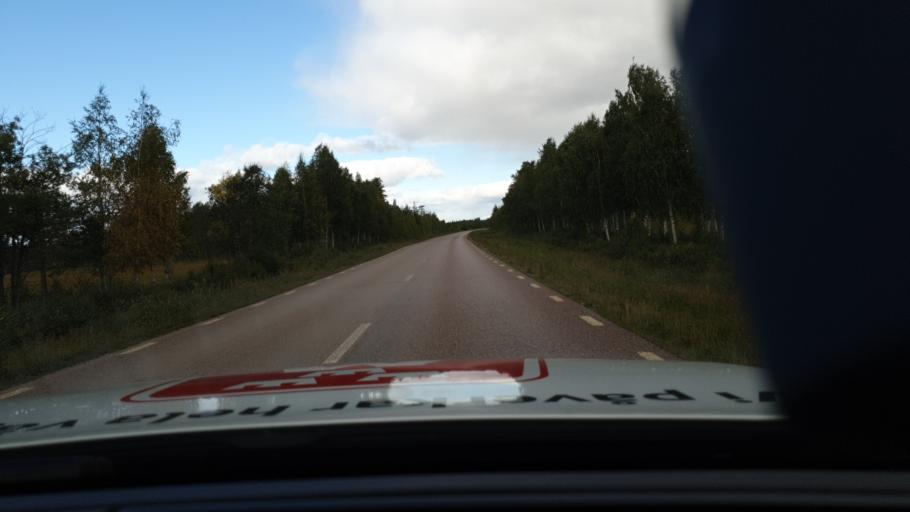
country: SE
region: Norrbotten
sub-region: Pajala Kommun
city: Pajala
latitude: 67.2435
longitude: 22.7796
